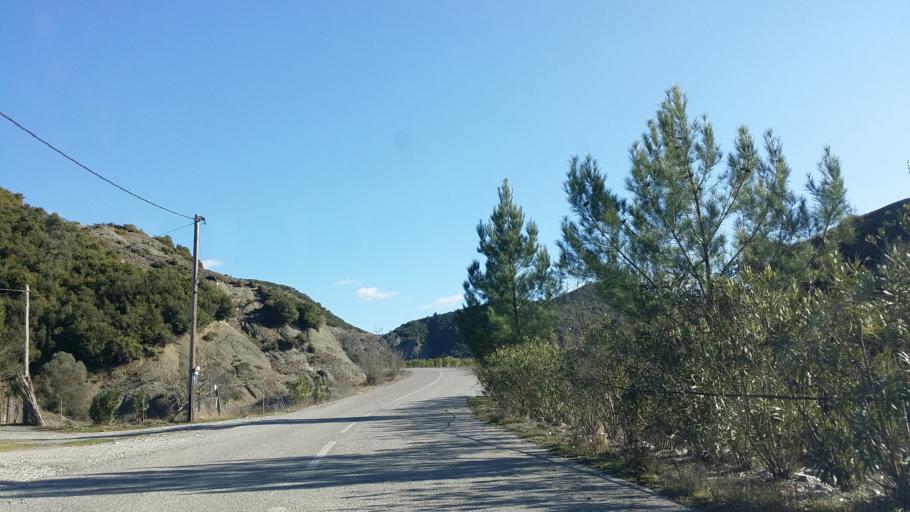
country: GR
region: Central Greece
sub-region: Nomos Evrytanias
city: Kerasochori
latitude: 39.0076
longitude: 21.5256
